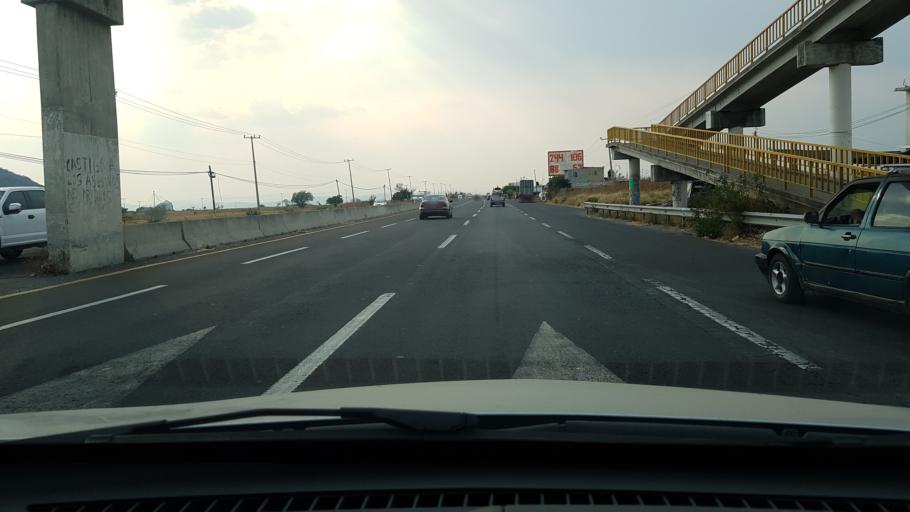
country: MX
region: Morelos
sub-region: Ayala
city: Unidad Habitacional Mariano Matamoros
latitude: 18.7516
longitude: -98.8531
